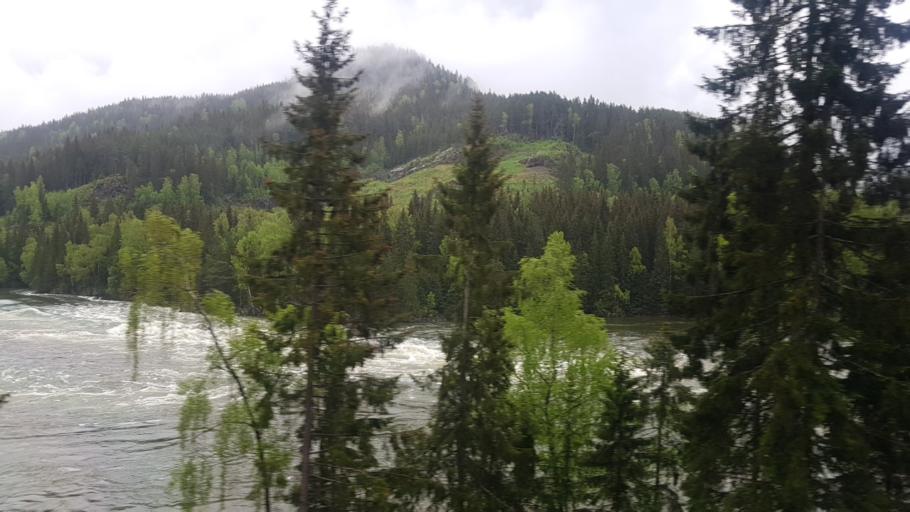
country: NO
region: Oppland
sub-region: Oyer
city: Tretten
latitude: 61.3105
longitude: 10.2927
